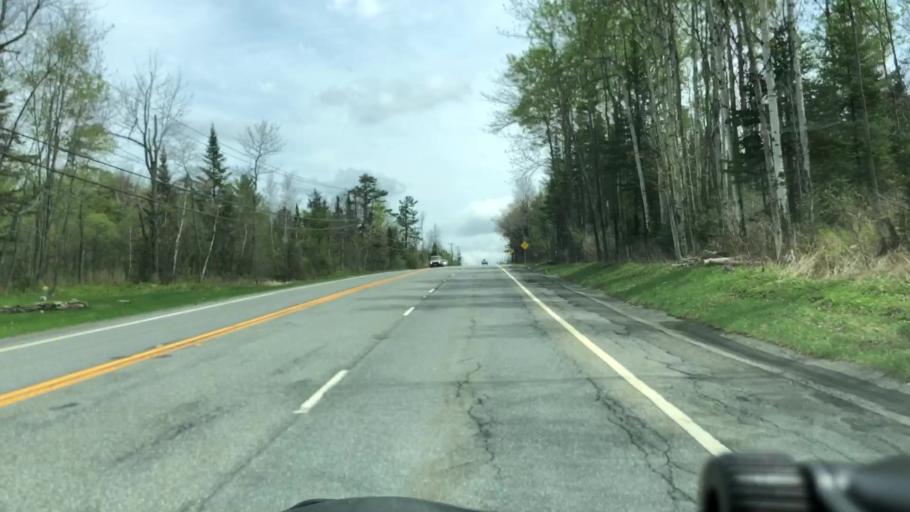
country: US
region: Massachusetts
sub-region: Berkshire County
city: Hinsdale
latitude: 42.5047
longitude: -73.0959
